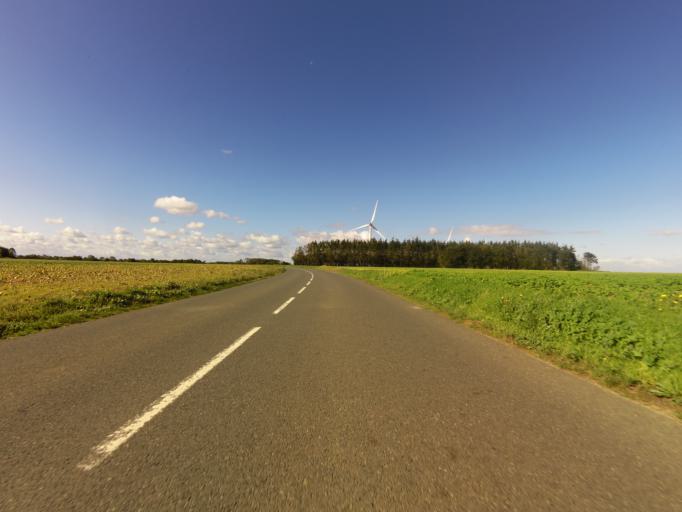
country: FR
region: Lower Normandy
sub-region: Departement du Calvados
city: Canon
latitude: 49.0459
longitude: -0.1433
